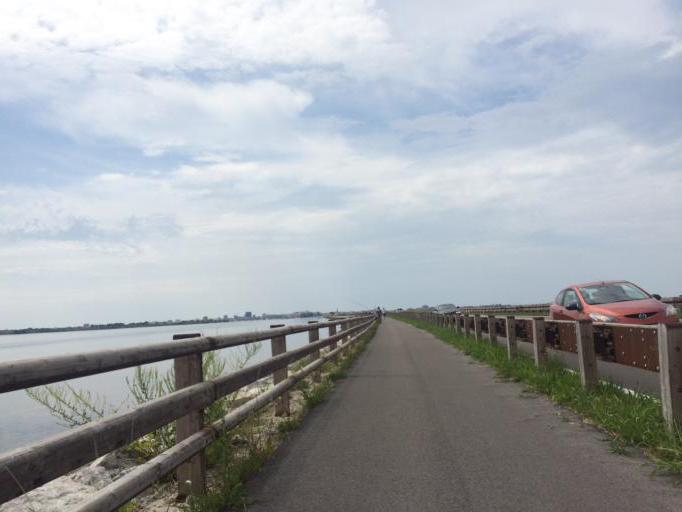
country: IT
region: Friuli Venezia Giulia
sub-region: Provincia di Gorizia
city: Grado
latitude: 45.7067
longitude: 13.3827
